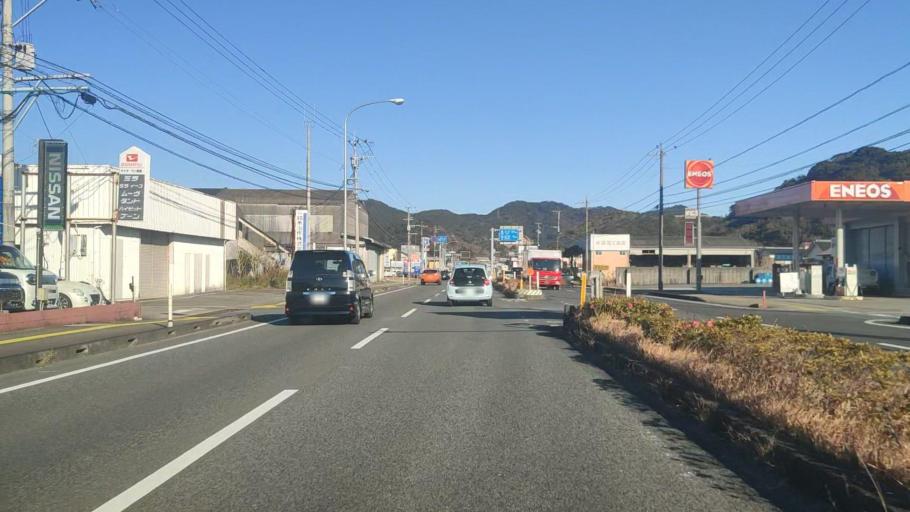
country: JP
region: Miyazaki
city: Nobeoka
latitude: 32.4897
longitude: 131.6642
